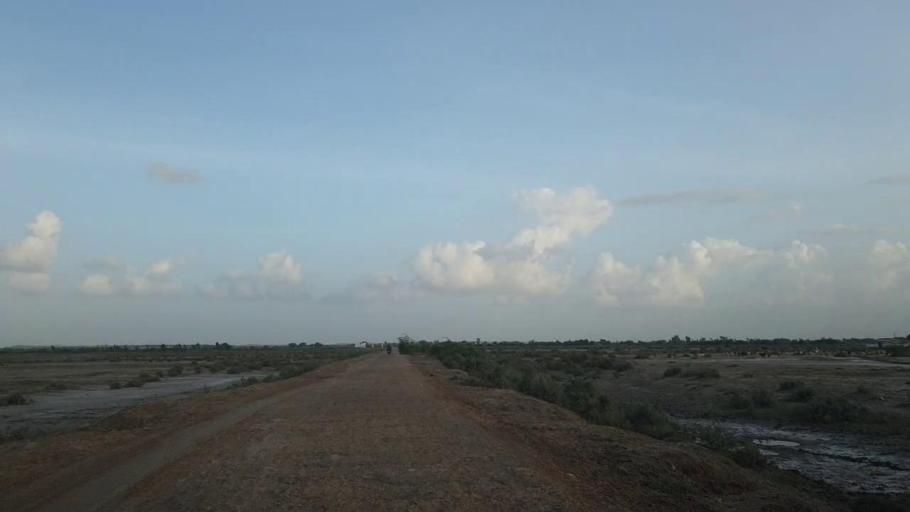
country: PK
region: Sindh
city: Kadhan
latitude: 24.5541
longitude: 69.1232
